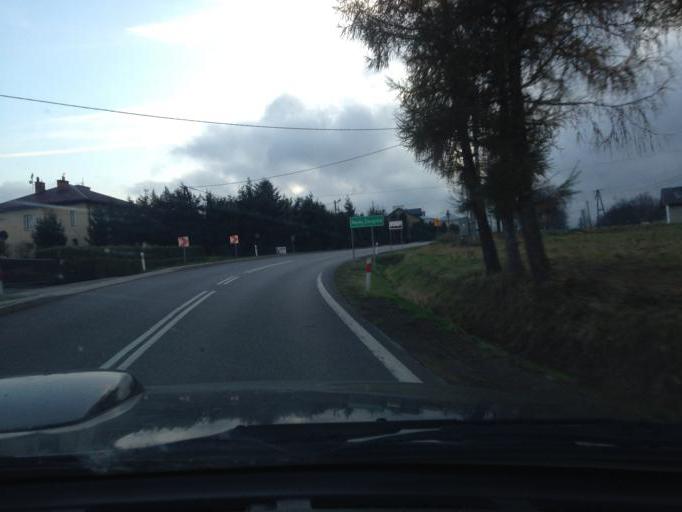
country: PL
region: Subcarpathian Voivodeship
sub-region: Powiat jasielski
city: Nowy Zmigrod
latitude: 49.6195
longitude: 21.5392
